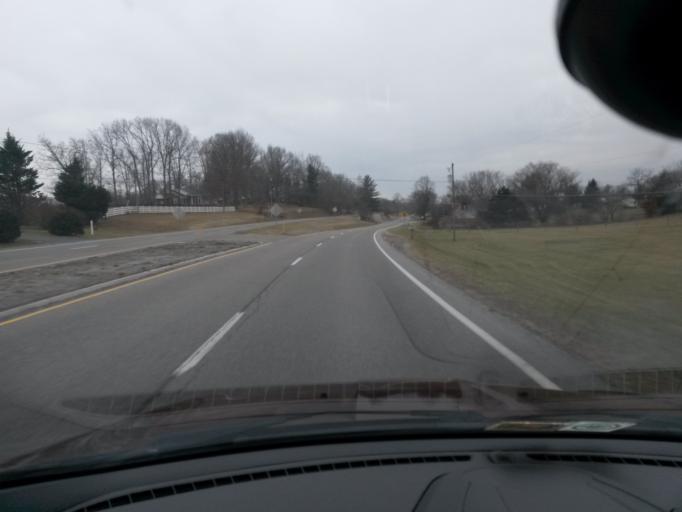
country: US
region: Virginia
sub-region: Augusta County
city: Stuarts Draft
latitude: 37.9437
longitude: -79.1856
